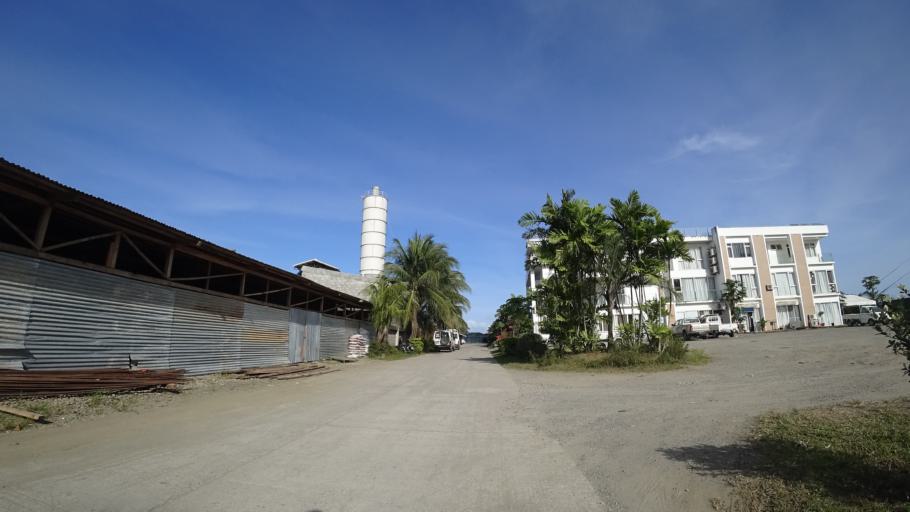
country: PH
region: Eastern Visayas
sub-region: Province of Leyte
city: Pawing
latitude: 11.1918
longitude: 124.9921
